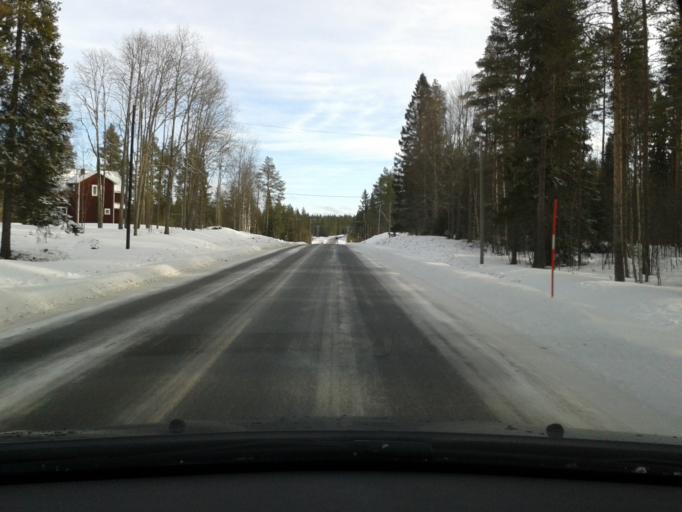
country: SE
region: Vaesterbotten
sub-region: Vilhelmina Kommun
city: Vilhelmina
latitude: 64.6470
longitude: 16.5324
